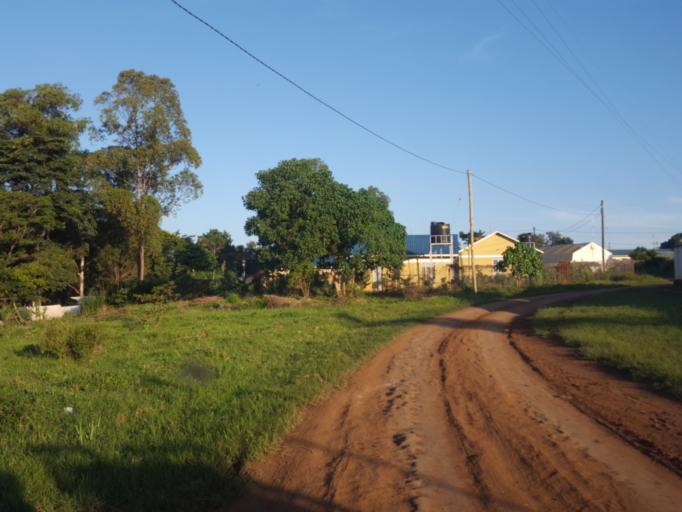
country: UG
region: Western Region
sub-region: Kibale District
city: Kagadi
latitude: 1.1907
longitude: 30.7812
